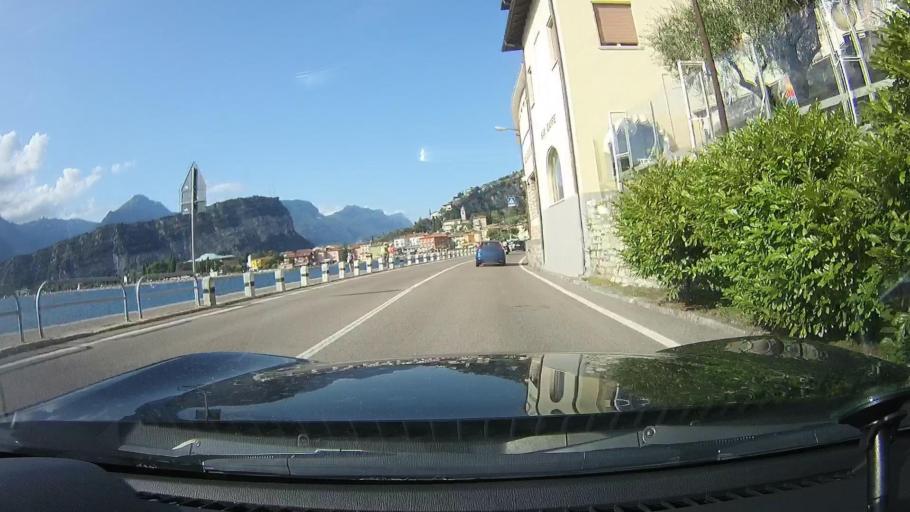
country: IT
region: Trentino-Alto Adige
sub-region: Provincia di Trento
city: Torbole sul Garda
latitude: 45.8651
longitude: 10.8755
